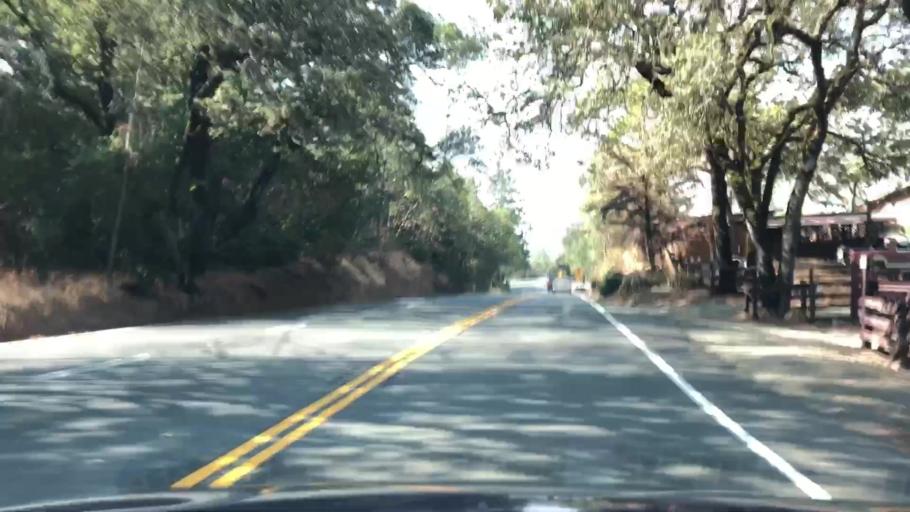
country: US
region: California
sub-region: Napa County
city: Calistoga
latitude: 38.6352
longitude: -122.6015
